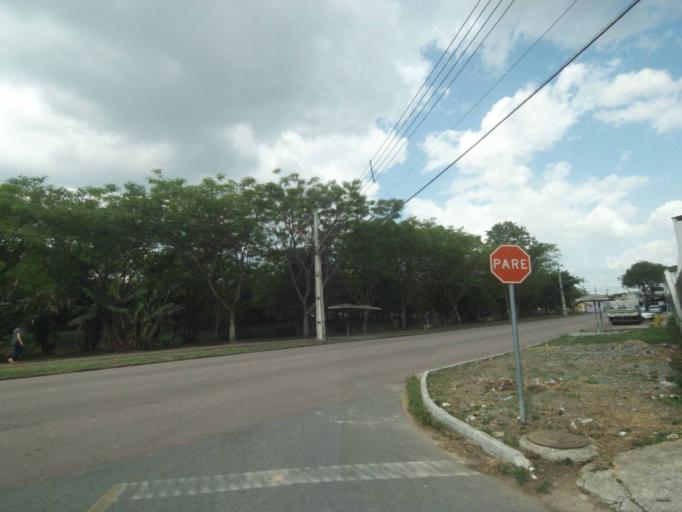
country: BR
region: Parana
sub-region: Sao Jose Dos Pinhais
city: Sao Jose dos Pinhais
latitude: -25.5282
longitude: -49.2620
